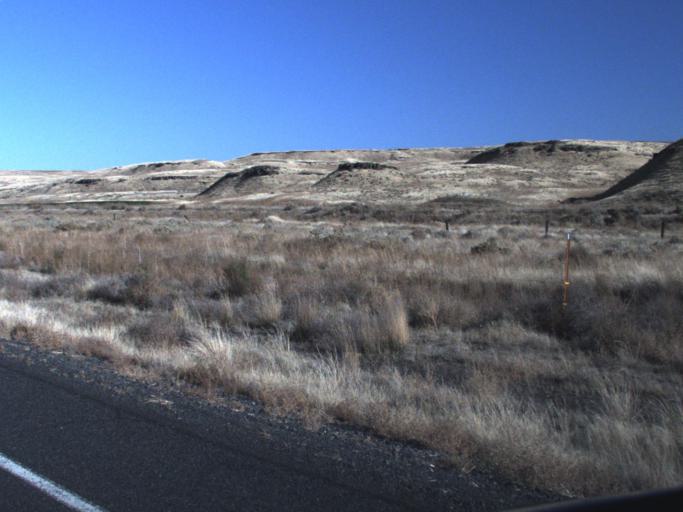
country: US
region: Washington
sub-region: Franklin County
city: Connell
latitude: 46.6730
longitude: -118.4649
